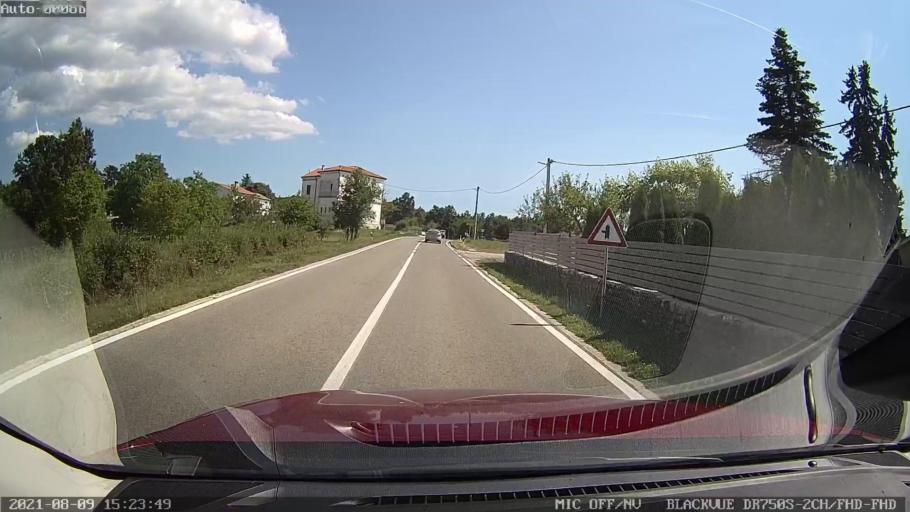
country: HR
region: Istarska
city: Pazin
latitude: 45.1802
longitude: 13.9042
